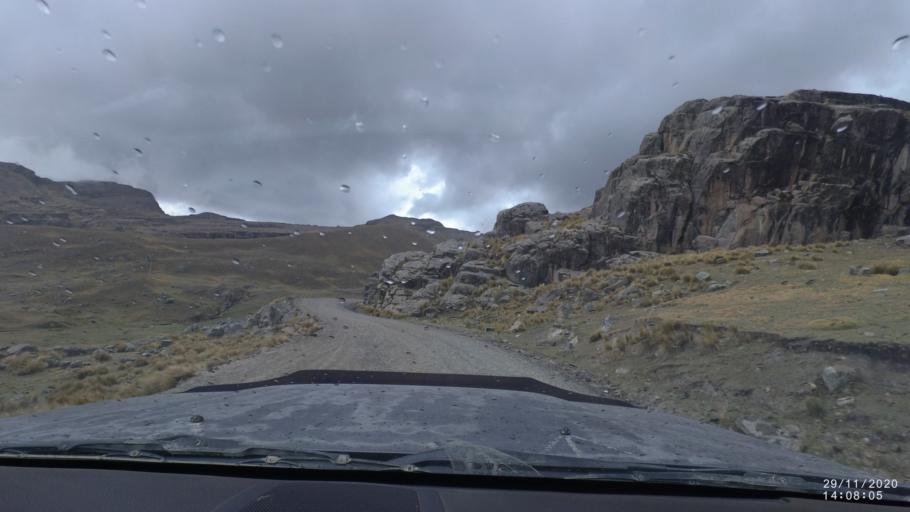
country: BO
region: Cochabamba
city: Sipe Sipe
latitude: -17.2216
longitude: -66.3851
